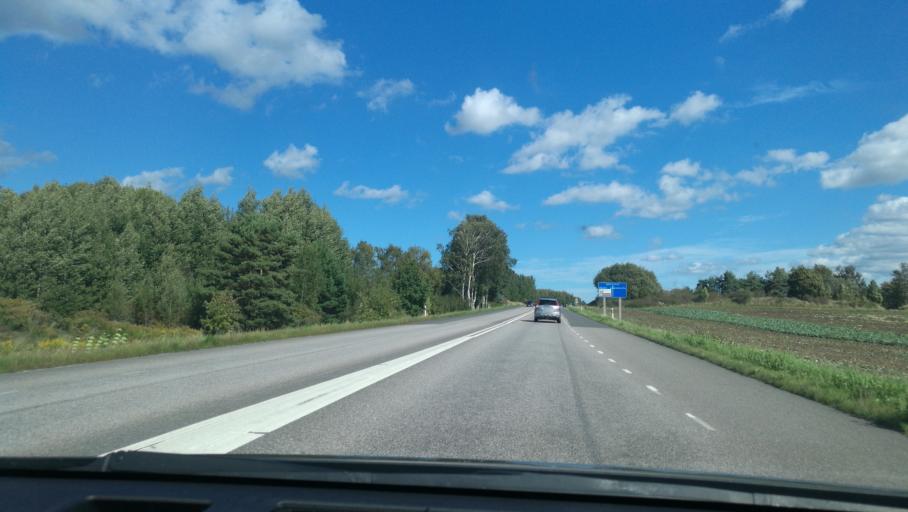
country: SE
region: Vaestra Goetaland
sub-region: Gotene Kommun
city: Kallby
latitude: 58.5014
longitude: 13.3057
